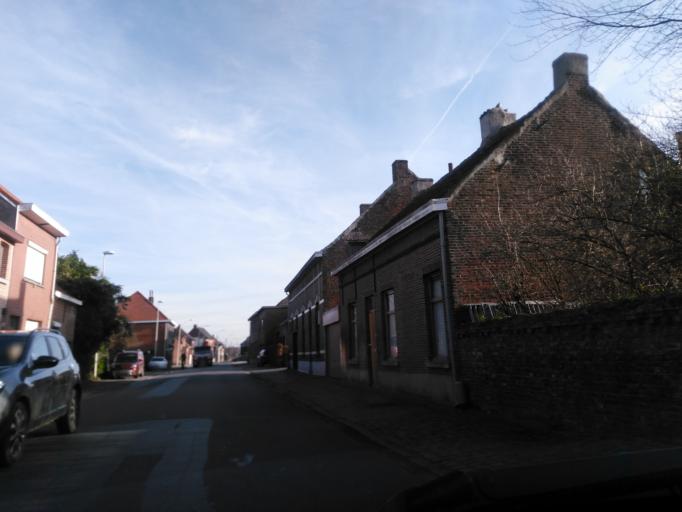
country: BE
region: Flanders
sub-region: Provincie Oost-Vlaanderen
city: Beveren
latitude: 51.2224
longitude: 4.2262
